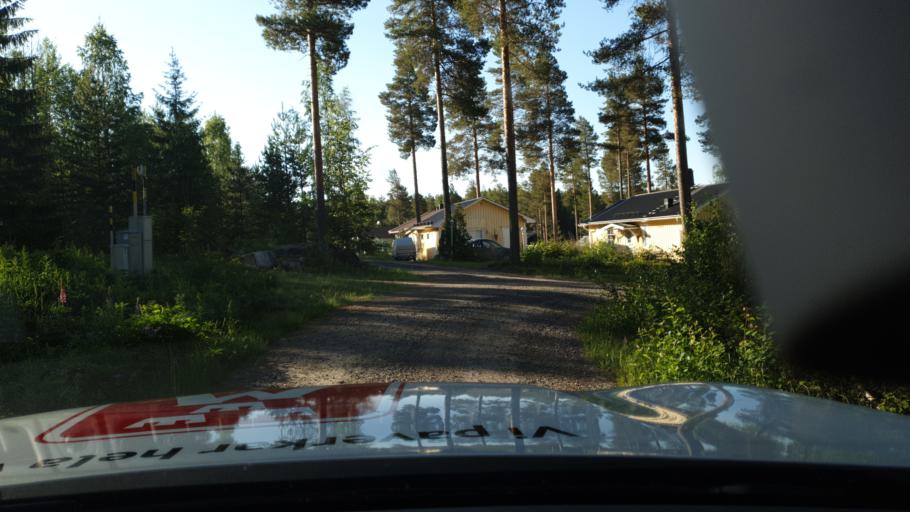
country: SE
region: Vaesterbotten
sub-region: Umea Kommun
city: Roback
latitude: 64.0048
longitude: 20.0845
